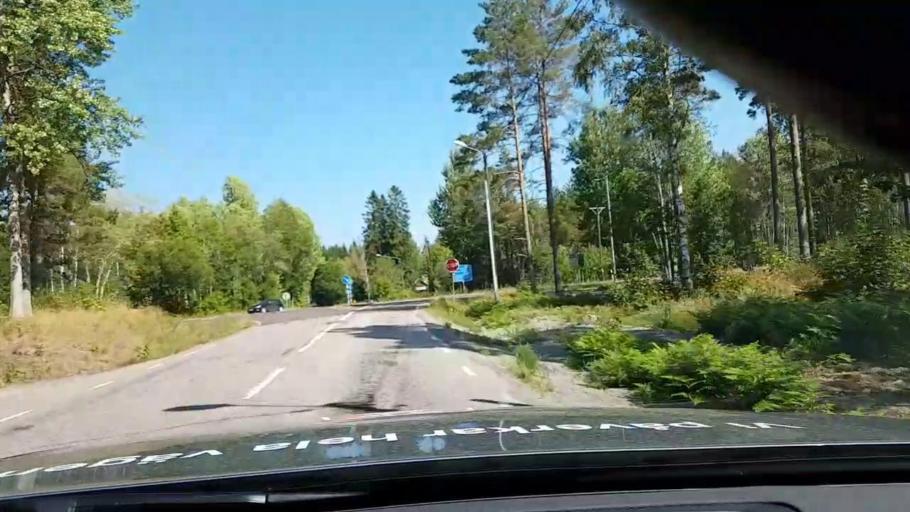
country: SE
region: Kalmar
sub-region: Hultsfreds Kommun
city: Virserum
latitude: 57.1385
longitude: 15.6597
